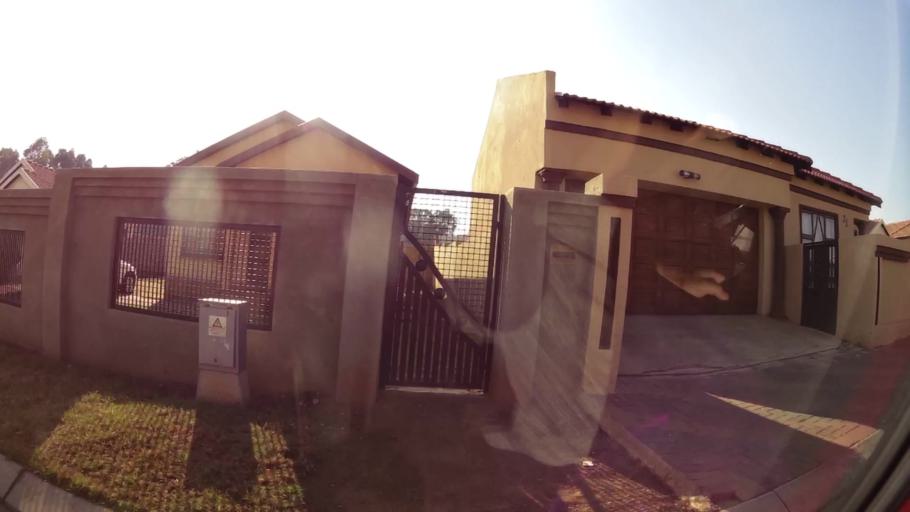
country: ZA
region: Gauteng
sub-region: City of Johannesburg Metropolitan Municipality
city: Soweto
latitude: -26.2855
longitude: 27.9503
